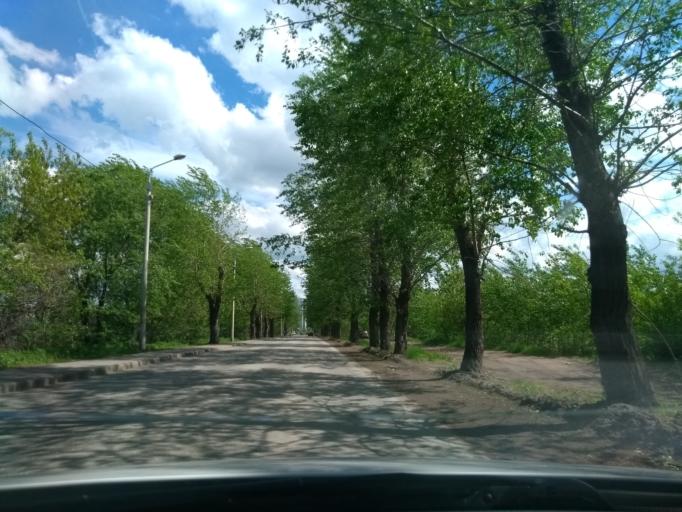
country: RU
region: Perm
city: Kondratovo
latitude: 58.0038
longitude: 56.1273
